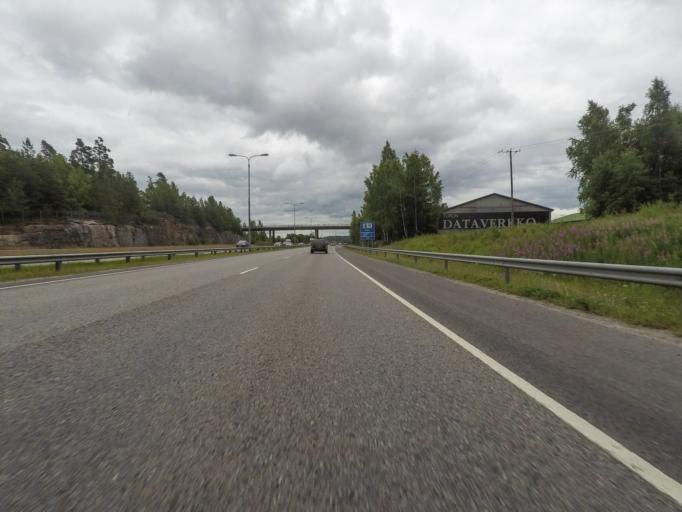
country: FI
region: Varsinais-Suomi
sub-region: Turku
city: Turku
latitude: 60.4948
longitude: 22.3051
